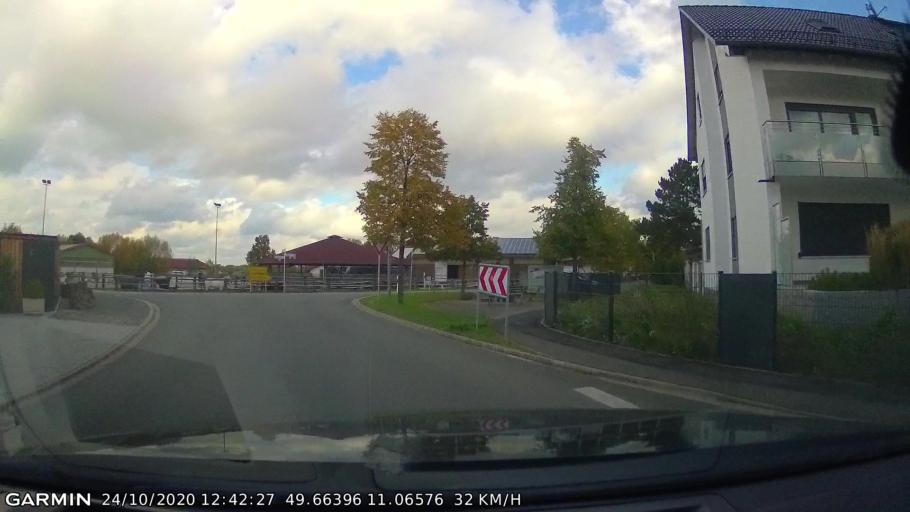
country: DE
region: Bavaria
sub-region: Upper Franconia
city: Poxdorf
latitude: 49.6640
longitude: 11.0658
